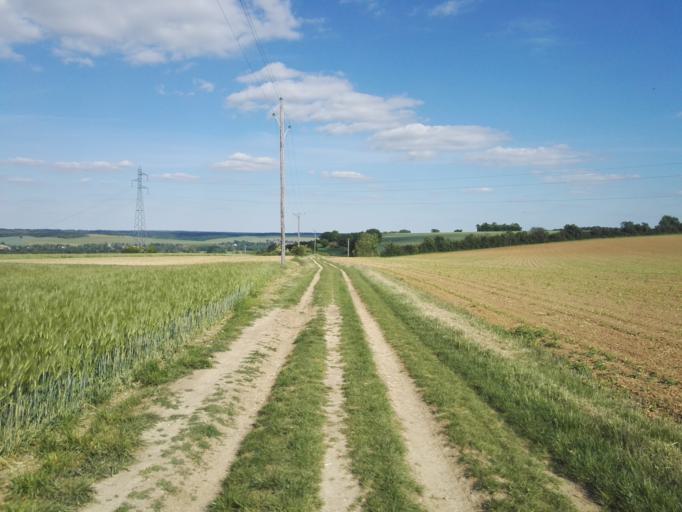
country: FR
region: Haute-Normandie
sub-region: Departement de l'Eure
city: Pacy-sur-Eure
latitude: 48.9887
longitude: 1.3748
